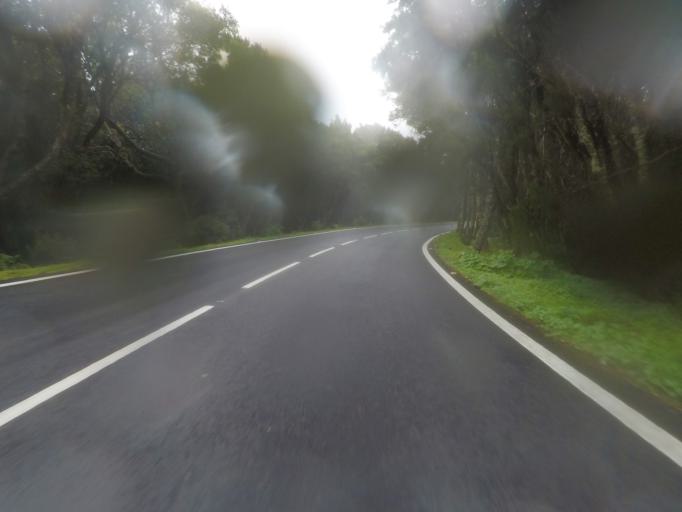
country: ES
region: Canary Islands
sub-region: Provincia de Santa Cruz de Tenerife
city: Vallehermosa
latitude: 28.1341
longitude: -17.2798
